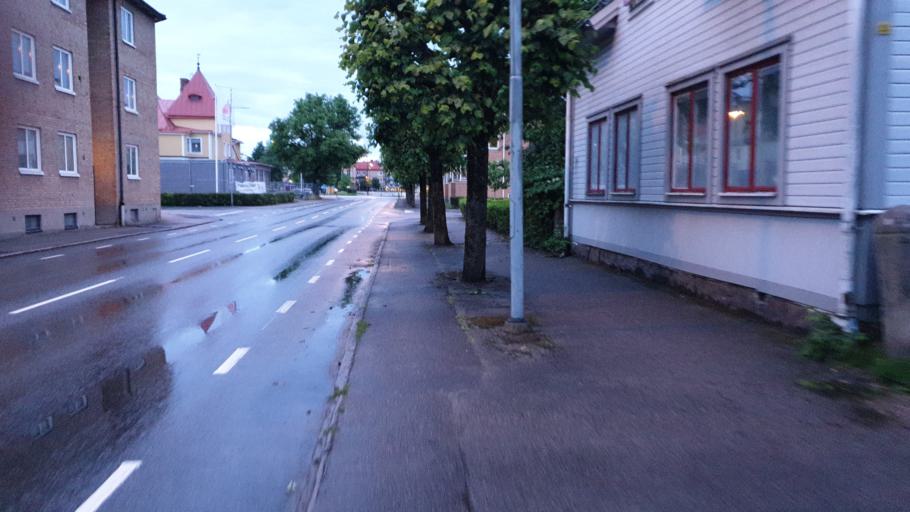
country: SE
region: Kronoberg
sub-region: Ljungby Kommun
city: Ljungby
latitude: 56.8306
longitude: 13.9397
